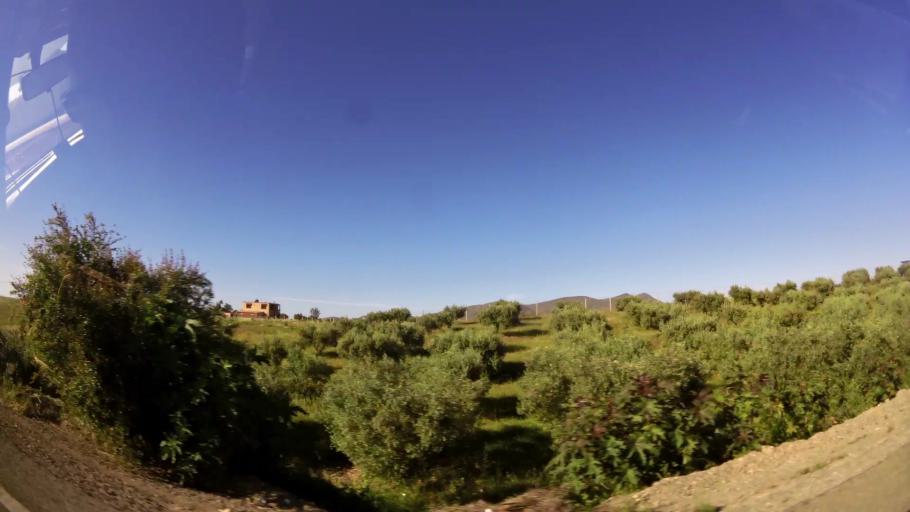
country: MA
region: Oriental
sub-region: Berkane-Taourirt
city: Ahfir
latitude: 34.9782
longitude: -2.1342
